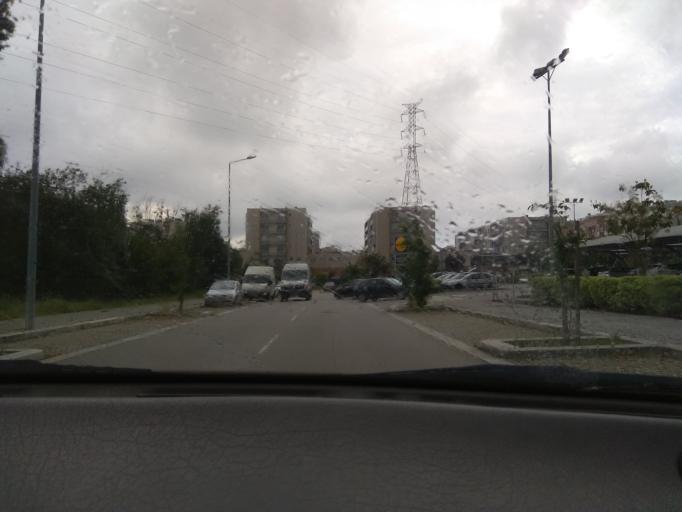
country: PT
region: Porto
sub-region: Maia
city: Leca do Bailio
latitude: 41.2267
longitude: -8.6104
